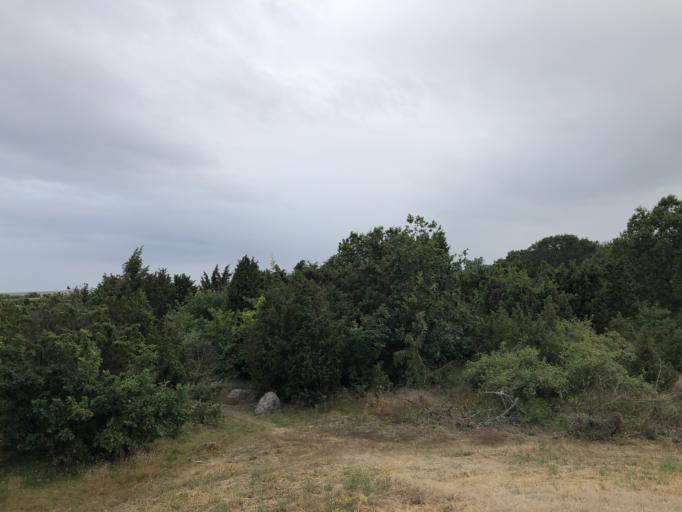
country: SE
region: Kalmar
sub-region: Kalmar Kommun
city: Kalmar
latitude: 56.6324
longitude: 16.3183
